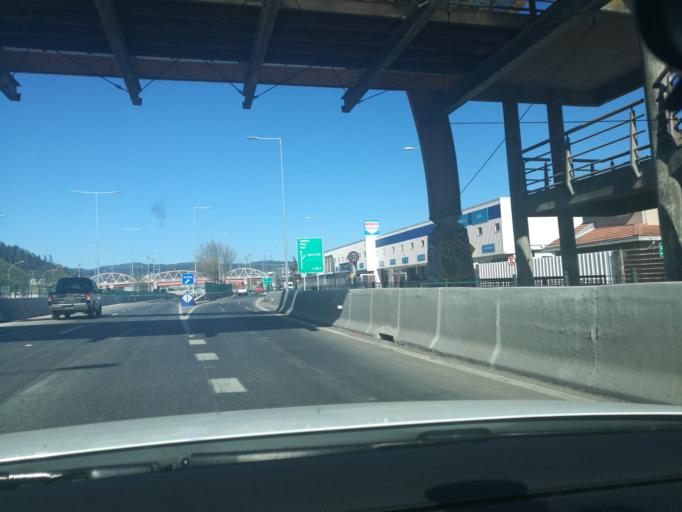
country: CL
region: Biobio
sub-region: Provincia de Concepcion
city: Concepcion
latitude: -36.8090
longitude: -73.0304
